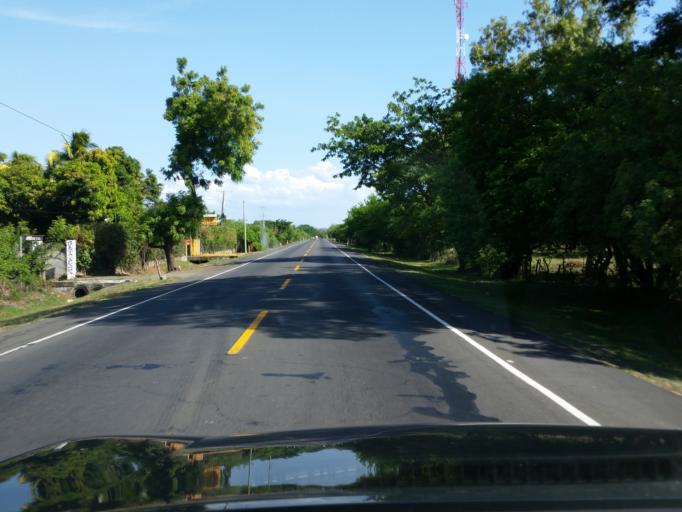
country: NI
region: Leon
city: Leon
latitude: 12.3698
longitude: -86.8389
